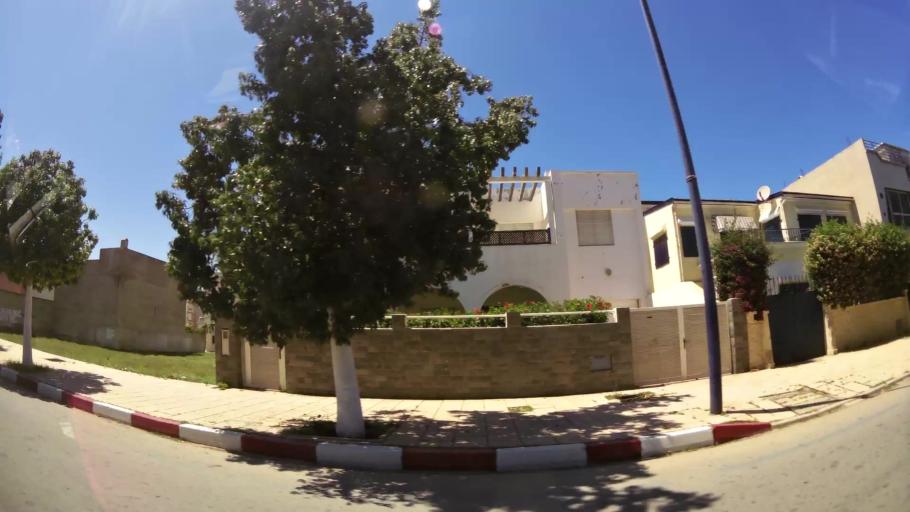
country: MA
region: Oriental
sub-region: Berkane-Taourirt
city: Madagh
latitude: 35.0753
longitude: -2.2172
